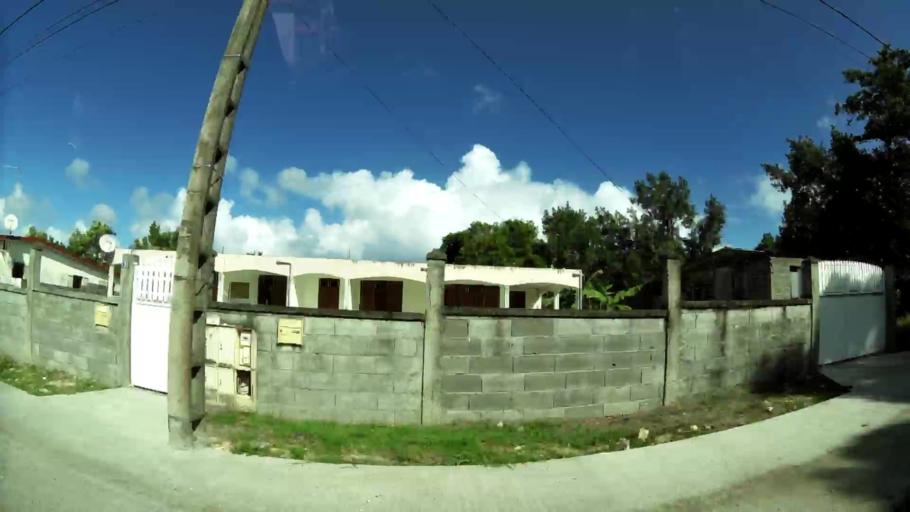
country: GP
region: Guadeloupe
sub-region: Guadeloupe
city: Port-Louis
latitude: 16.4189
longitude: -61.5260
